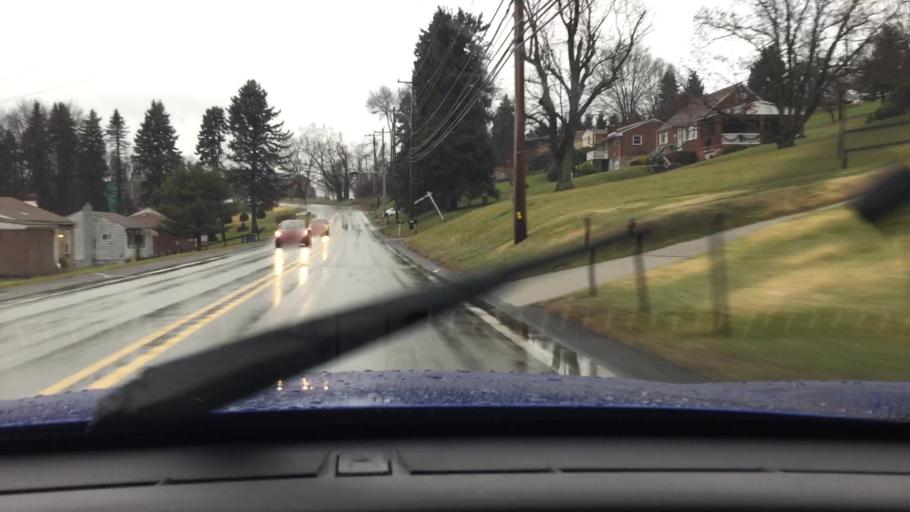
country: US
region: Pennsylvania
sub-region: Allegheny County
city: Wilson
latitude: 40.3139
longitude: -79.9169
